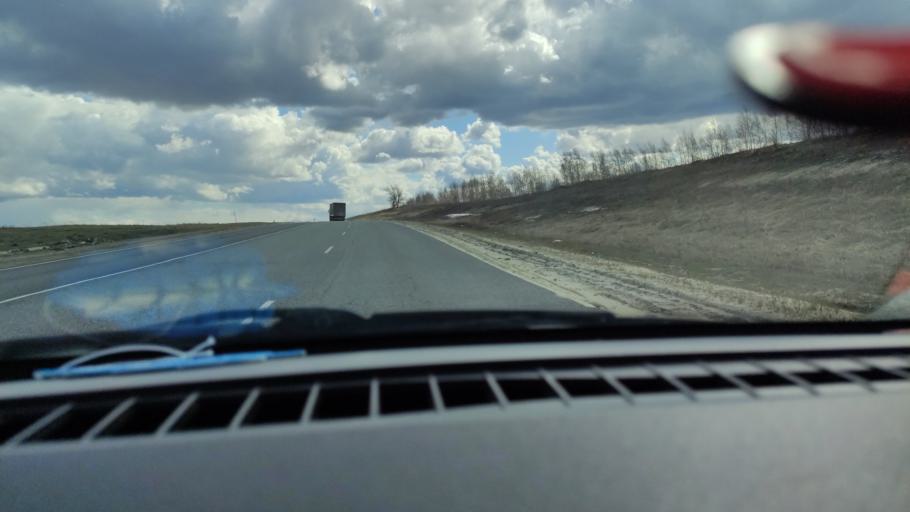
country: RU
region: Samara
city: Syzran'
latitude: 52.9570
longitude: 48.3075
